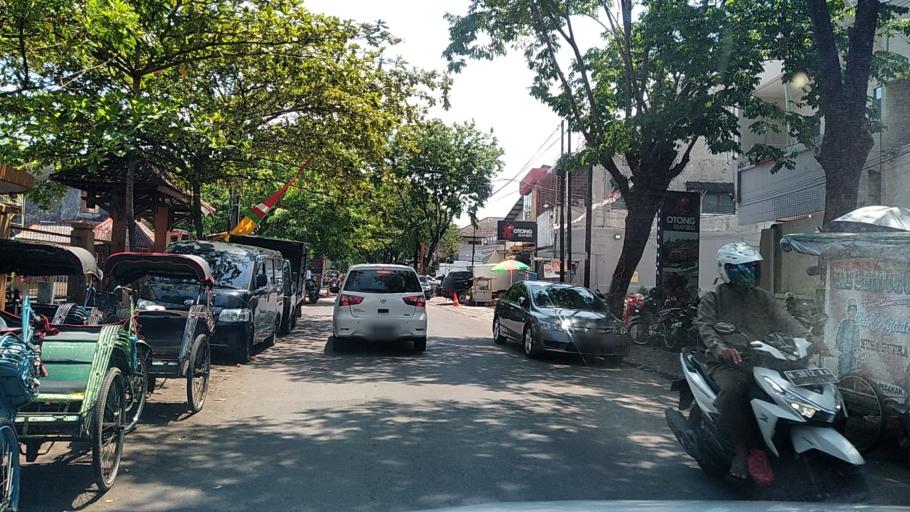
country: ID
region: Central Java
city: Semarang
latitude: -6.9814
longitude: 110.4269
